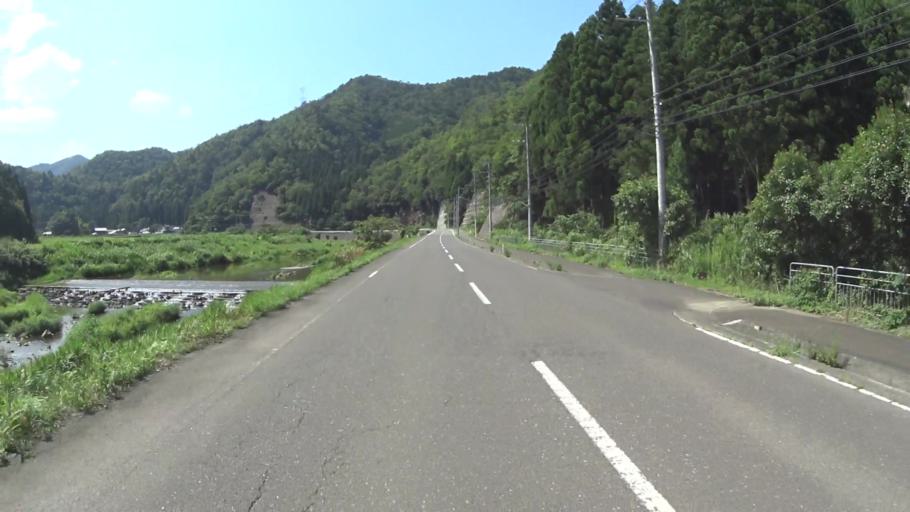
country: JP
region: Fukui
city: Obama
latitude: 35.4008
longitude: 135.6236
